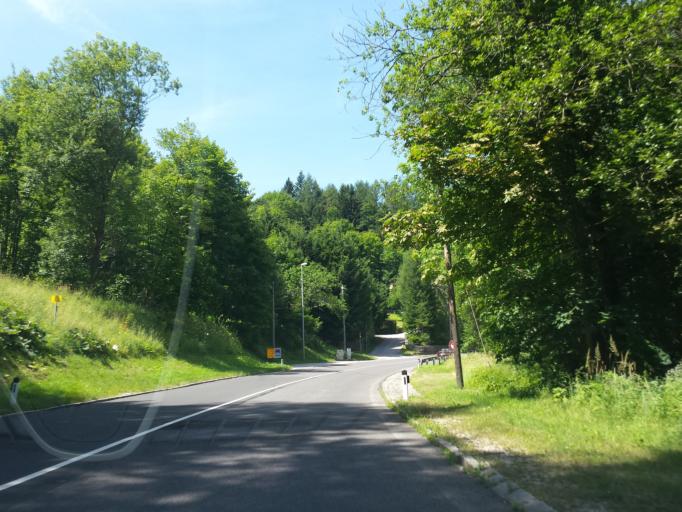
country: AT
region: Lower Austria
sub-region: Politischer Bezirk Neunkirchen
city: Semmering
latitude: 47.6317
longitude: 15.8342
